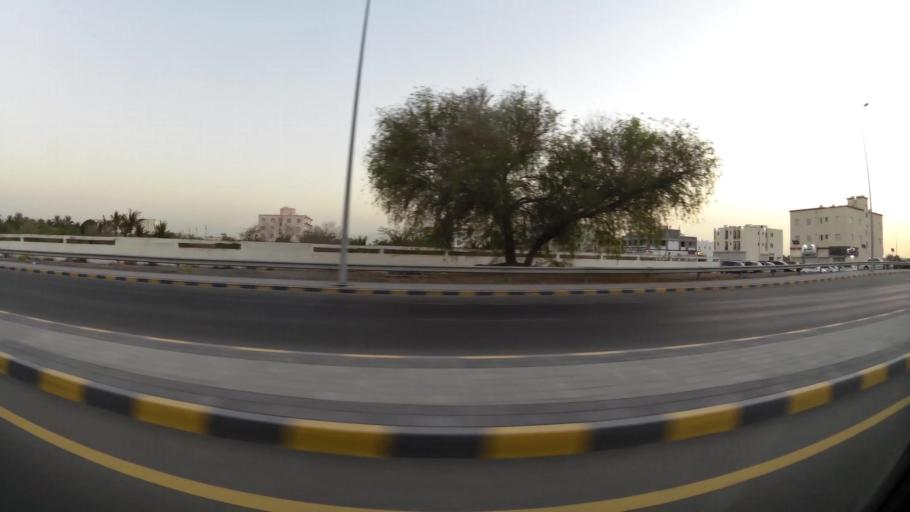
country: OM
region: Muhafazat Masqat
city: As Sib al Jadidah
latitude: 23.6655
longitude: 58.1947
